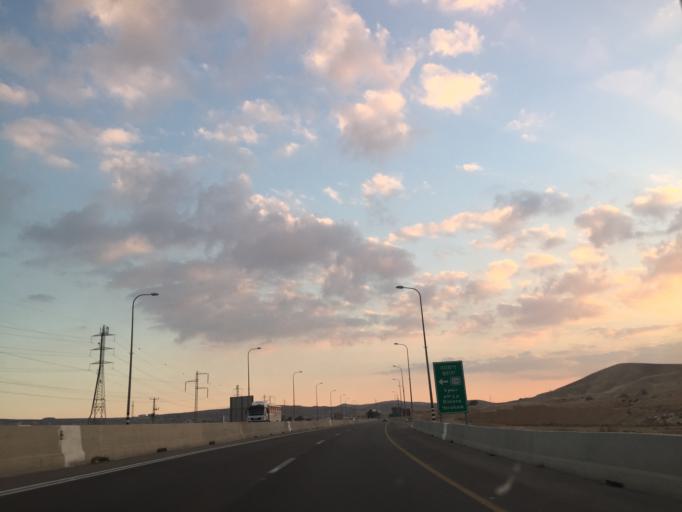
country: IL
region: Southern District
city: Yeroham
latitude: 31.0726
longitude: 34.8394
